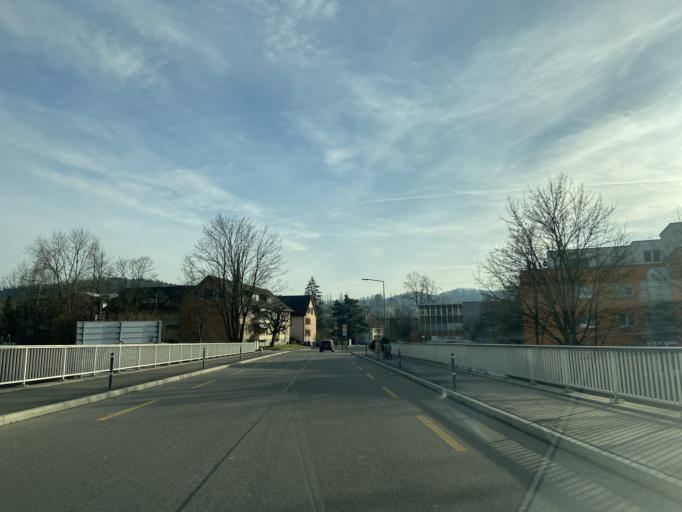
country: CH
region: Zurich
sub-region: Bezirk Winterthur
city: Wuelflingen (Kreis 6) / Lindenplatz
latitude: 47.5135
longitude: 8.6942
